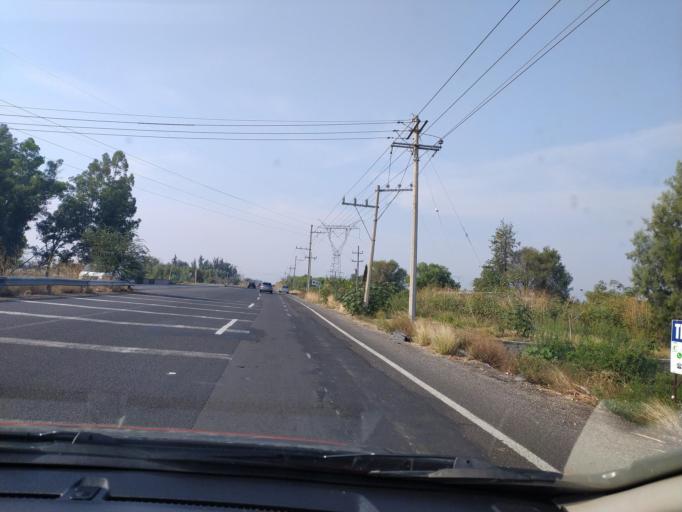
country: MX
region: Jalisco
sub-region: Acatlan de Juarez
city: Villa de los Ninos
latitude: 20.3938
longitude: -103.5935
